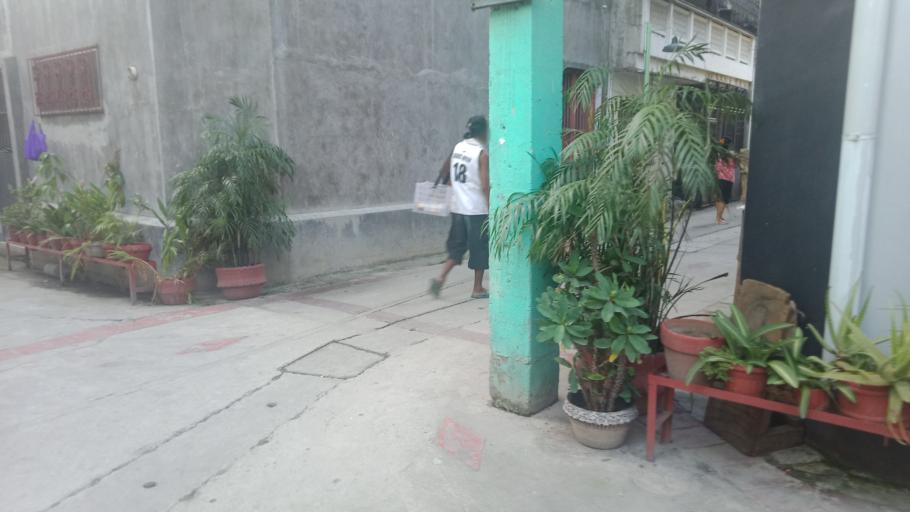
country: PH
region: Calabarzon
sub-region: Province of Rizal
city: Taguig
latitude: 14.5414
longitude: 121.1029
